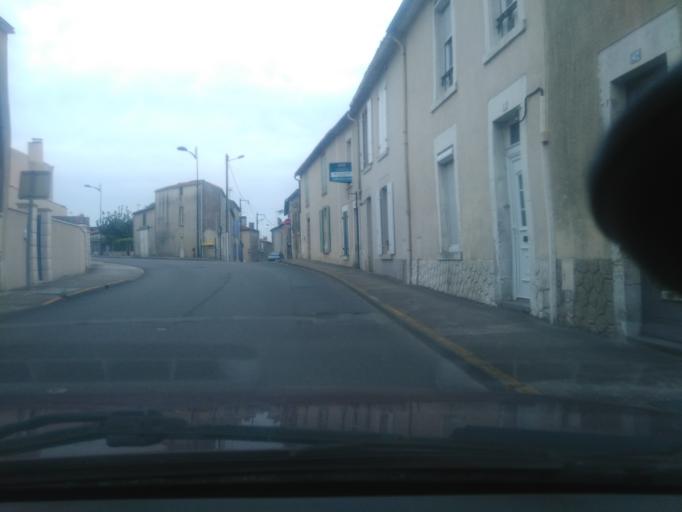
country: FR
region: Pays de la Loire
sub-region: Departement de la Vendee
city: La Chataigneraie
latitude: 46.6492
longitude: -0.7395
